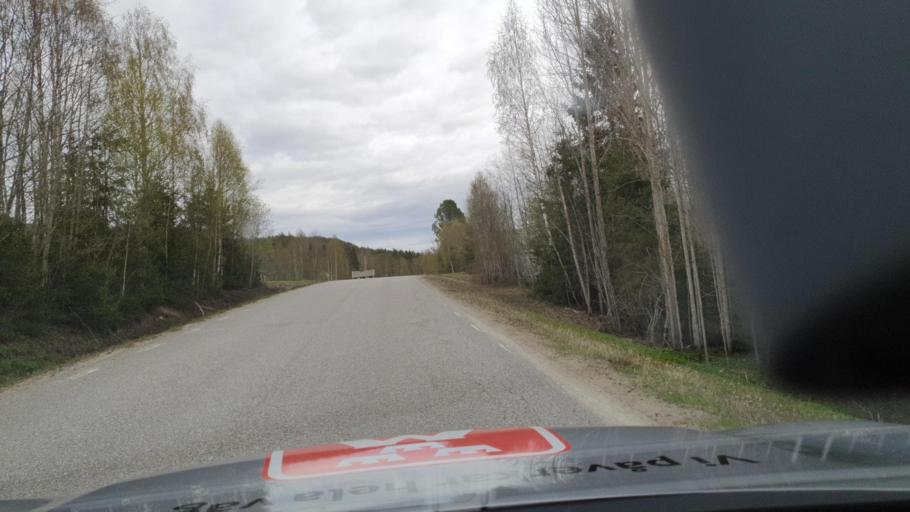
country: SE
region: Vaesternorrland
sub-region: OErnskoeldsviks Kommun
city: Ornskoldsvik
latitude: 63.6424
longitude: 18.7683
